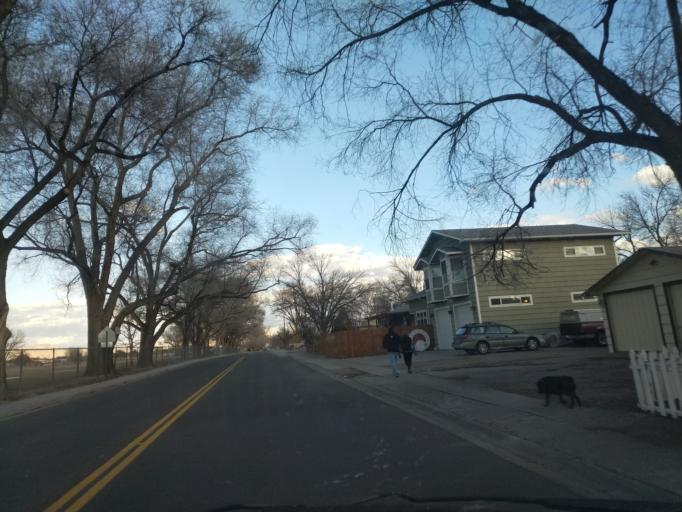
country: US
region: Colorado
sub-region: Mesa County
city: Grand Junction
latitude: 39.0734
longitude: -108.5464
